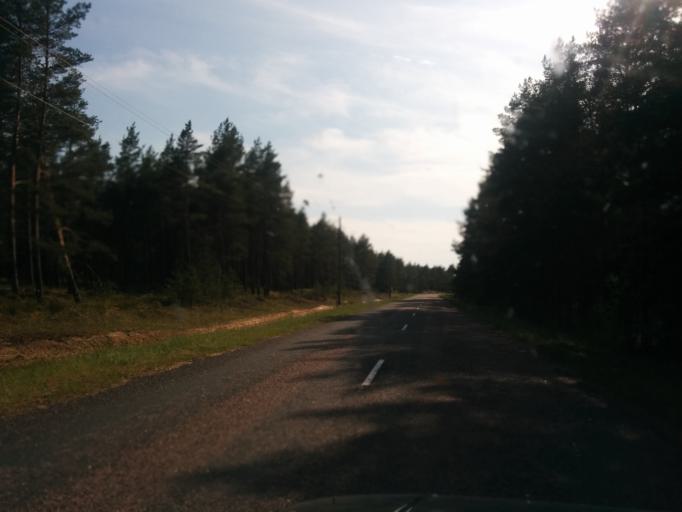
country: LV
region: Dundaga
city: Dundaga
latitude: 57.6584
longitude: 22.2829
